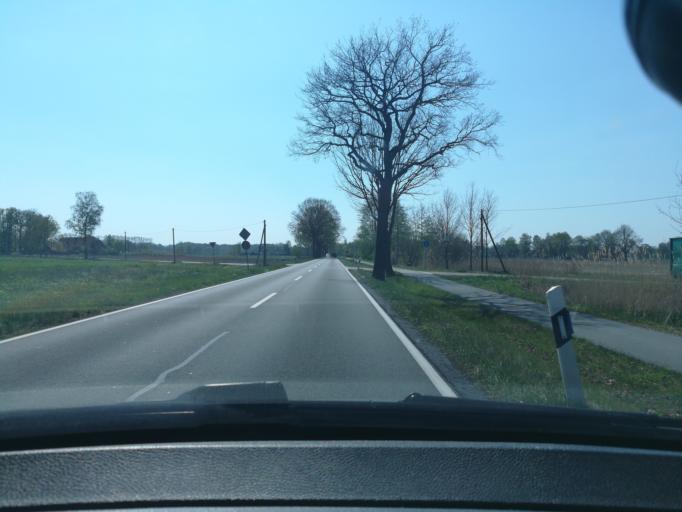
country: DE
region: North Rhine-Westphalia
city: Borgholzhausen
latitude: 52.0331
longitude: 8.2651
